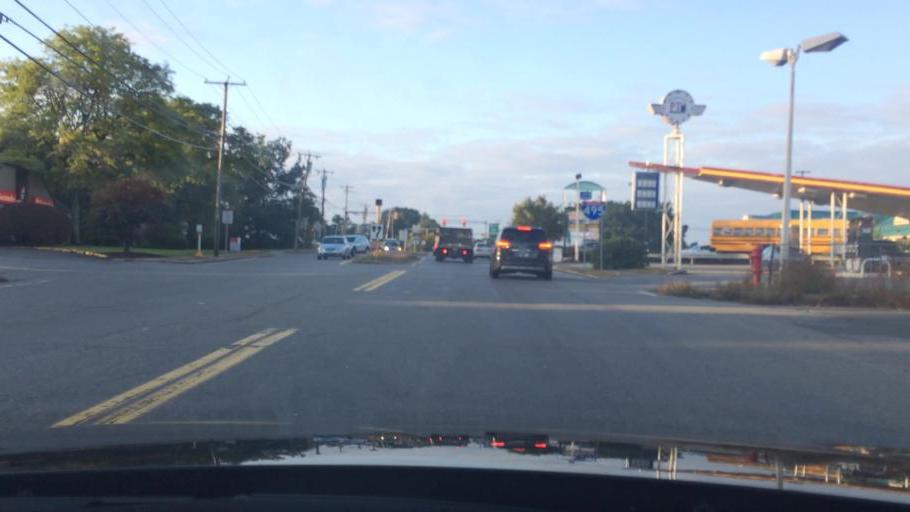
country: US
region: Massachusetts
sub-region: Essex County
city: North Andover
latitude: 42.7314
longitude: -71.1364
